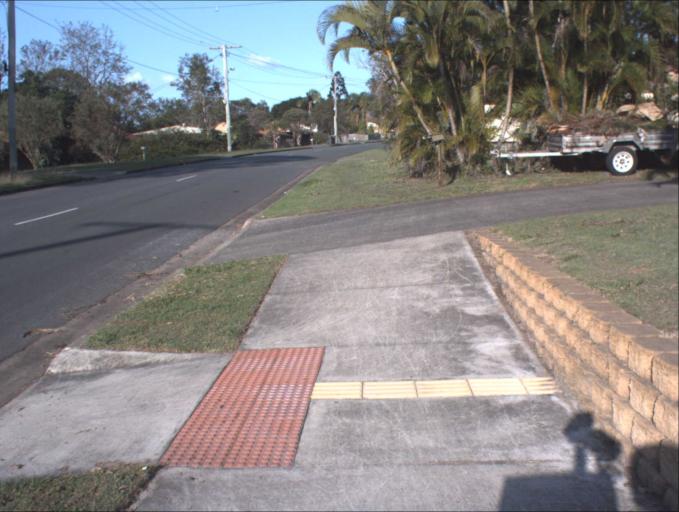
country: AU
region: Queensland
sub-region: Logan
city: Waterford West
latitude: -27.6924
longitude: 153.1591
